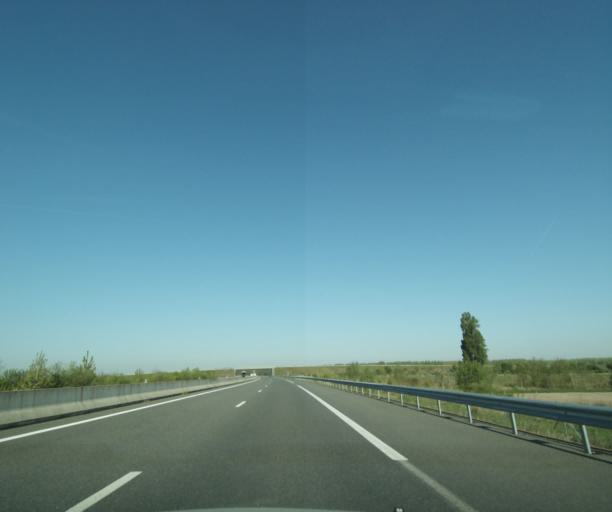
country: FR
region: Centre
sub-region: Departement du Loiret
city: Corbeilles
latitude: 48.0932
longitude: 2.5826
